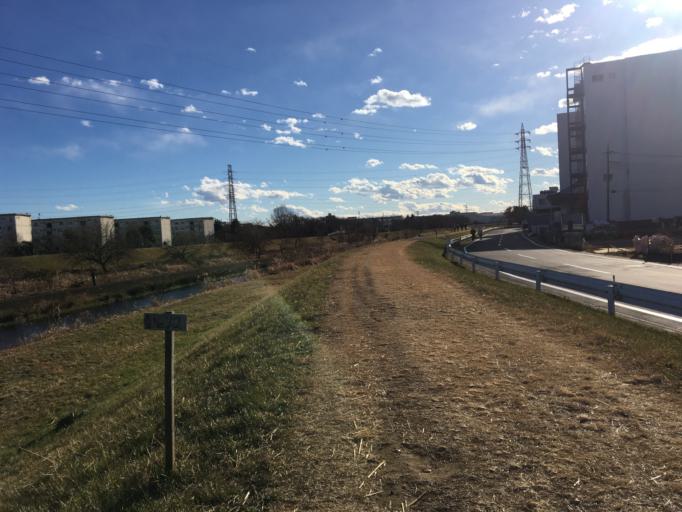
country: JP
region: Saitama
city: Shiki
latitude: 35.8227
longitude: 139.5536
